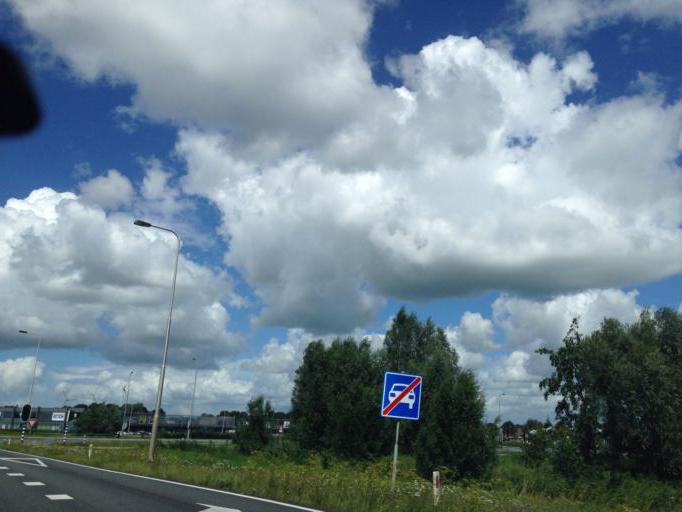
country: NL
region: Overijssel
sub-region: Gemeente Kampen
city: Kampen
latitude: 52.5545
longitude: 5.8840
